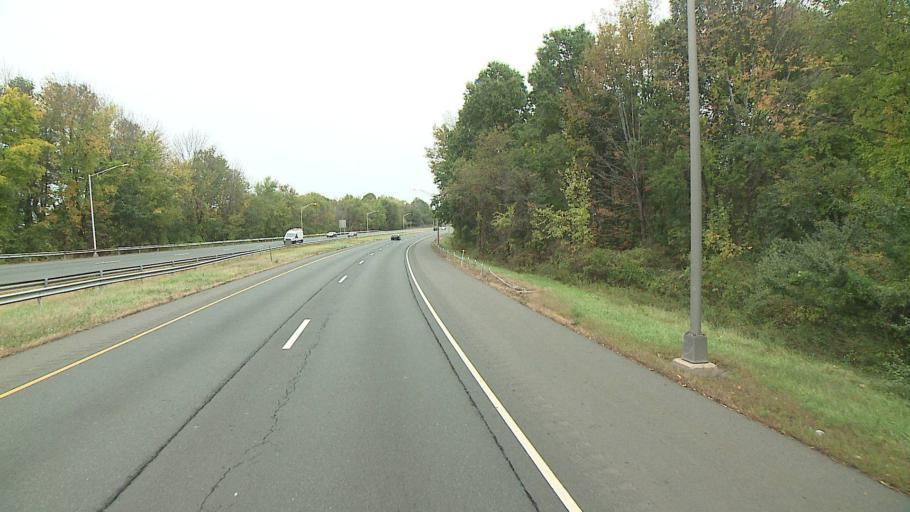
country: US
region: Connecticut
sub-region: Hartford County
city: Kensington
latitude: 41.6296
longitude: -72.7506
